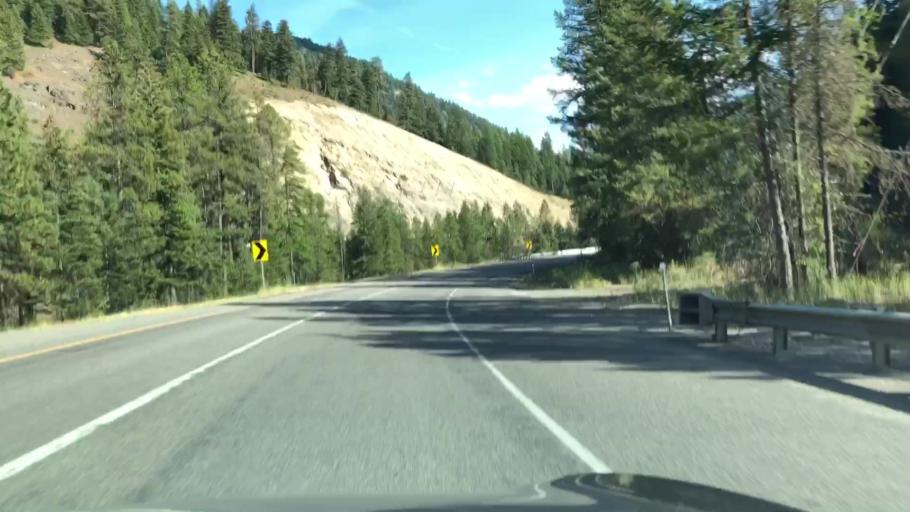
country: US
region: Montana
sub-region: Sanders County
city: Thompson Falls
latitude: 47.3311
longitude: -115.2605
